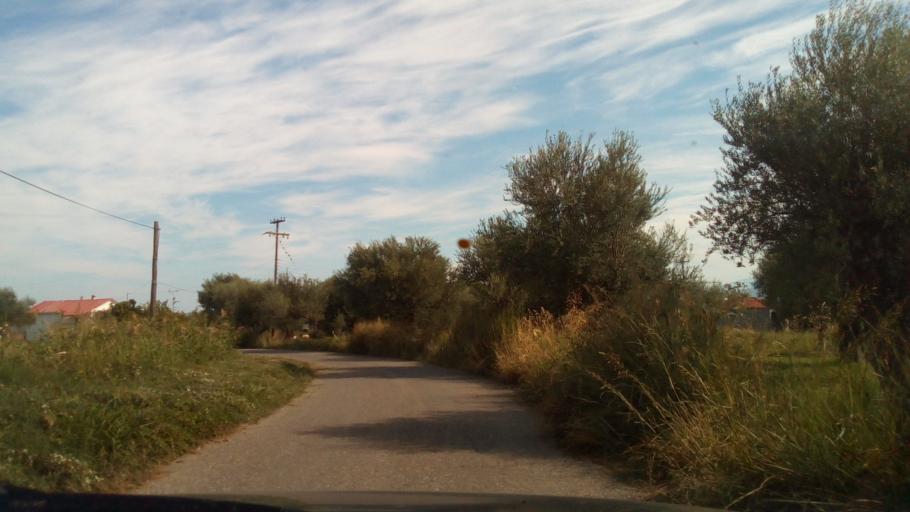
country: GR
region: West Greece
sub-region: Nomos Aitolias kai Akarnanias
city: Nafpaktos
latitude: 38.4027
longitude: 21.8966
